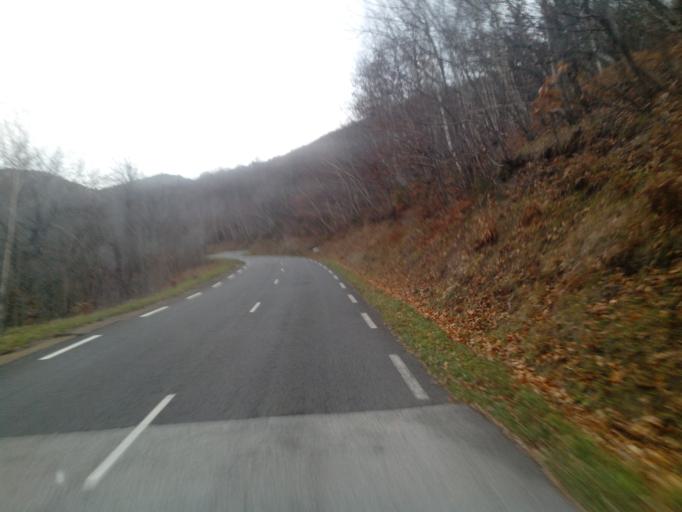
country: FR
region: Languedoc-Roussillon
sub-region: Departement de la Lozere
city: Florac
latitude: 44.2793
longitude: 3.5987
